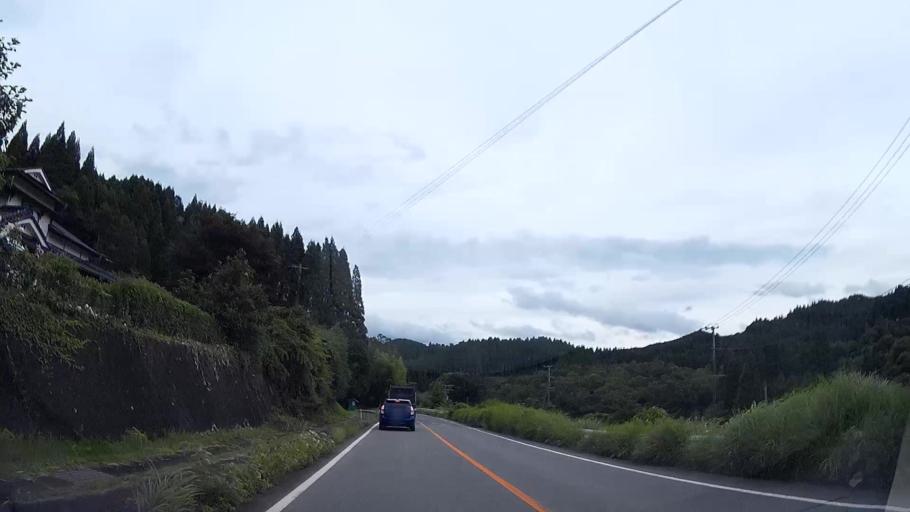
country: JP
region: Kumamoto
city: Aso
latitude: 33.1225
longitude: 131.0222
